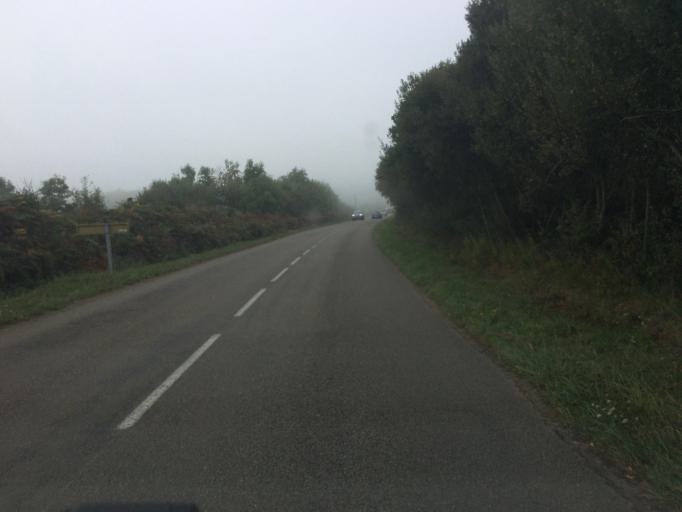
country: FR
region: Brittany
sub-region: Departement du Finistere
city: Plogoff
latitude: 48.0623
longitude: -4.6418
